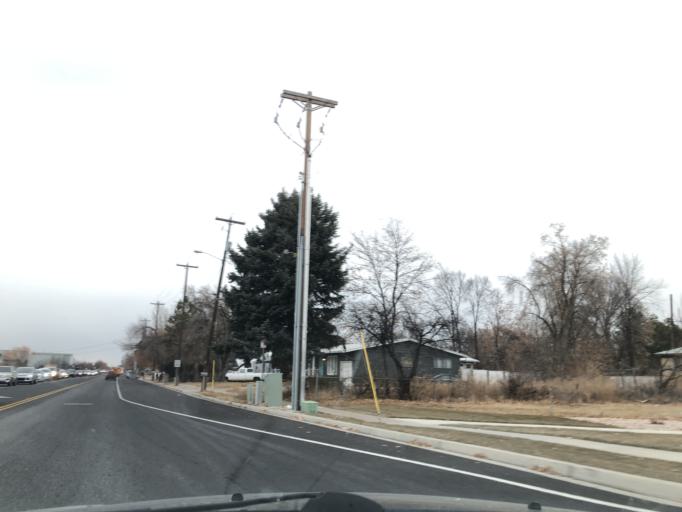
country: US
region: Utah
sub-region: Cache County
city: Logan
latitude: 41.7502
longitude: -111.8293
